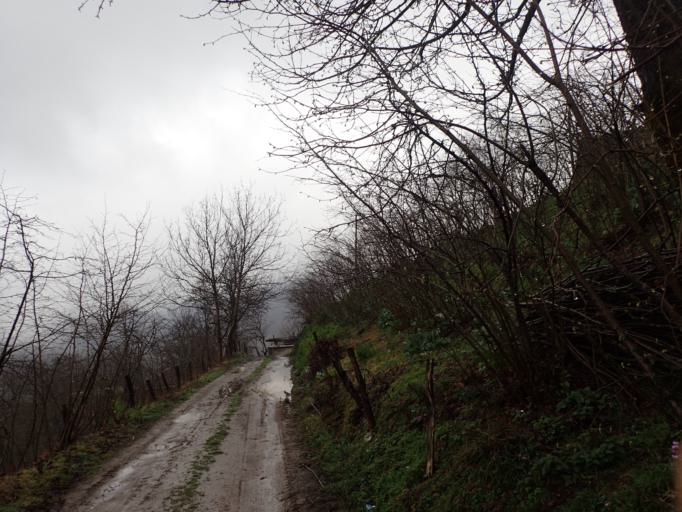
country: TR
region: Ordu
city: Camas
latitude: 40.9136
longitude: 37.5700
